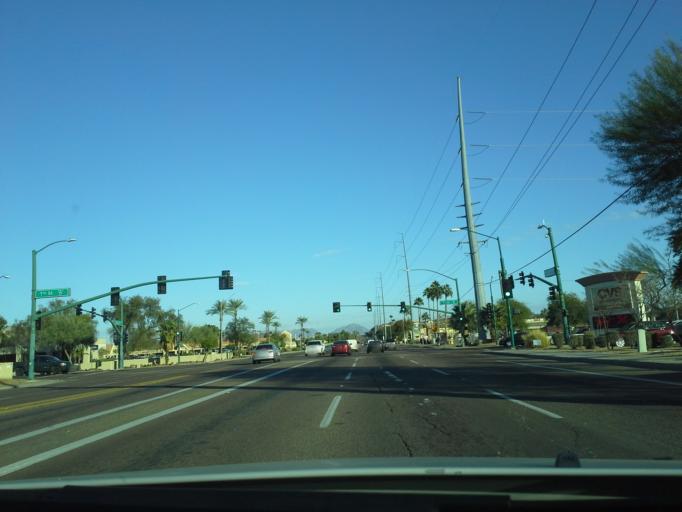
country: US
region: Arizona
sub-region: Maricopa County
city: Glendale
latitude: 33.6547
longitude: -112.0663
